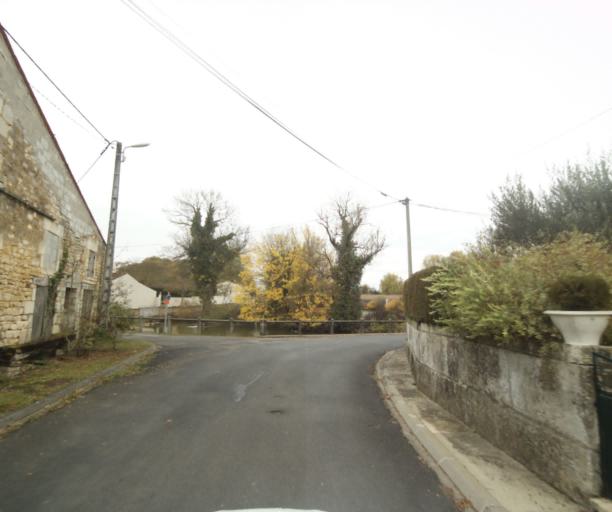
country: FR
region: Poitou-Charentes
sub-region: Departement de la Charente-Maritime
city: Chermignac
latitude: 45.7103
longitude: -0.6651
